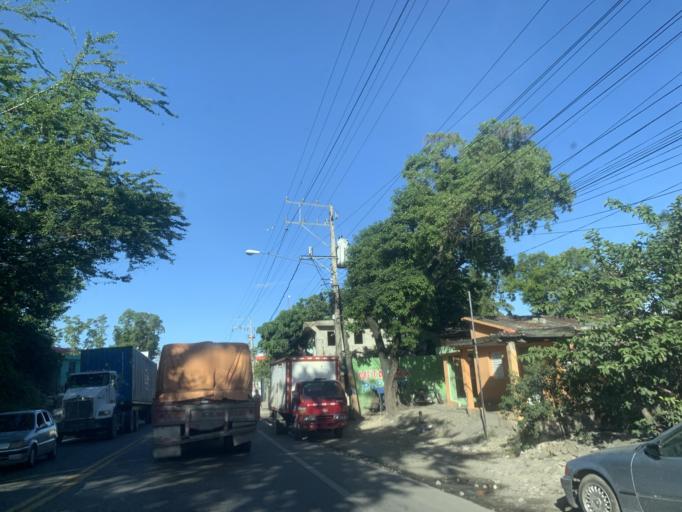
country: DO
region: San Cristobal
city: Bajos de Haina
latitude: 18.4288
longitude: -70.0312
